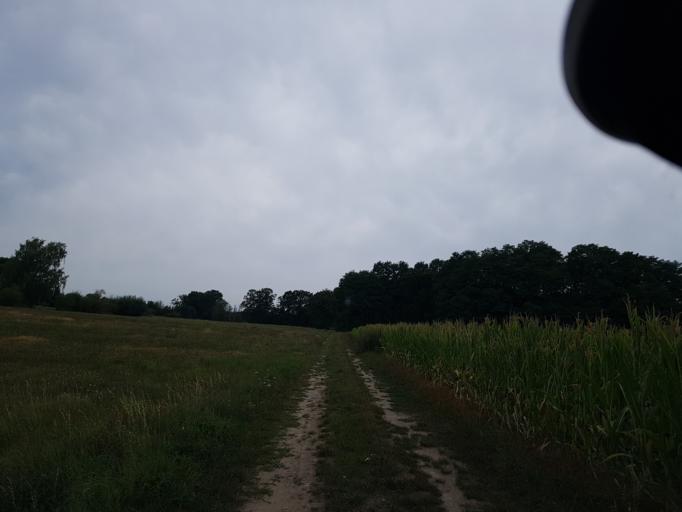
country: DE
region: Brandenburg
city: Finsterwalde
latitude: 51.6132
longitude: 13.6497
